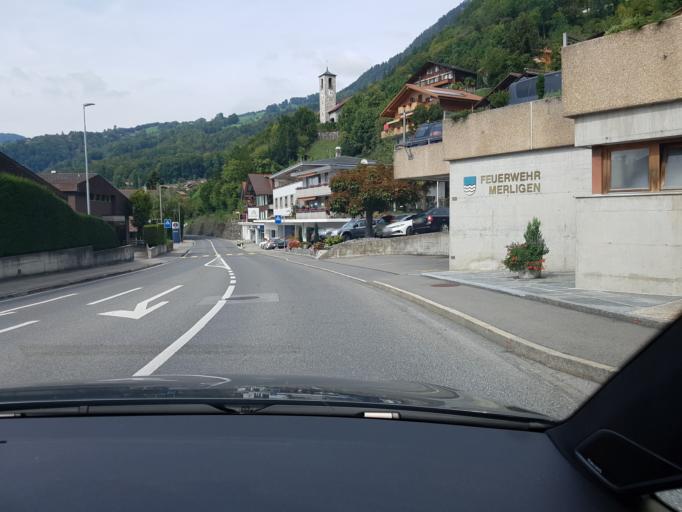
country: CH
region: Bern
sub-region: Thun District
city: Sigriswil
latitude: 46.6975
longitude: 7.7376
